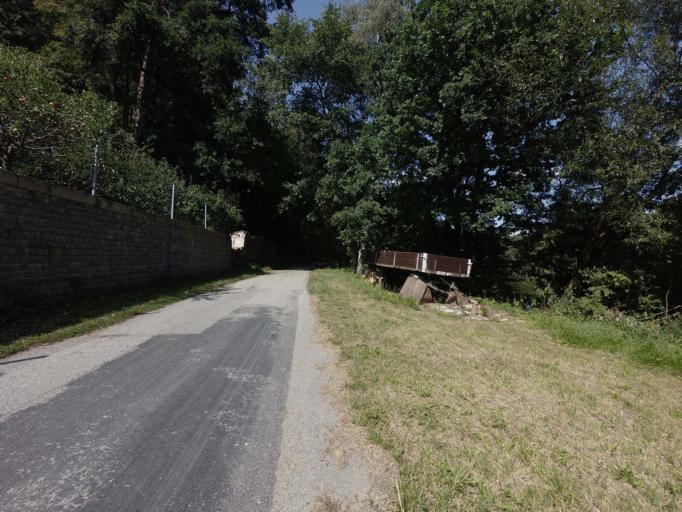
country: CZ
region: Jihocesky
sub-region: Okres Ceske Budejovice
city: Hluboka nad Vltavou
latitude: 49.0579
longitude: 14.4419
